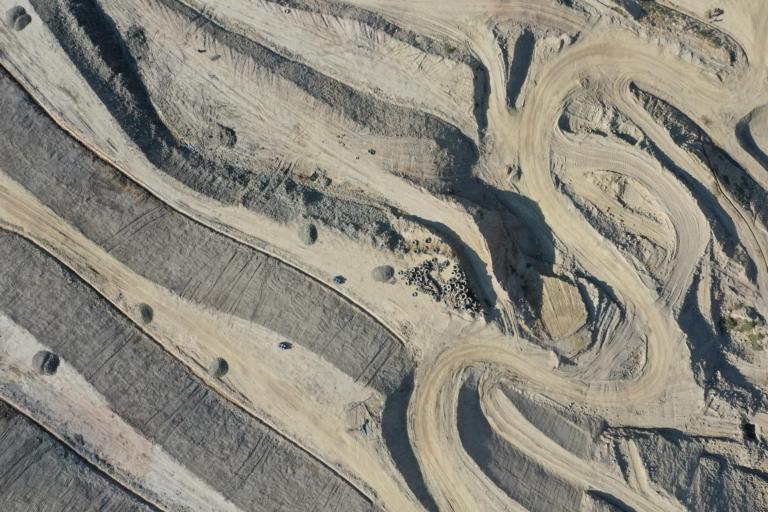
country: BO
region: La Paz
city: La Paz
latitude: -16.5577
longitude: -68.1266
